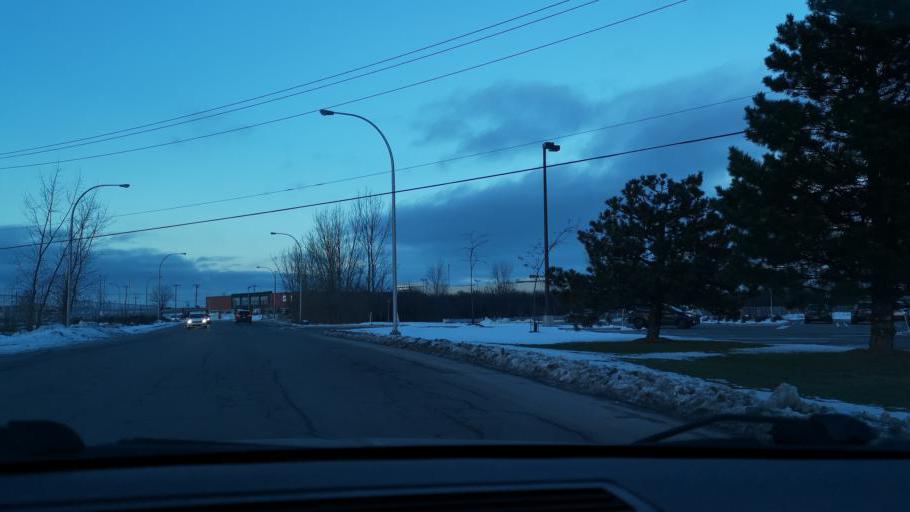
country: CA
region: Quebec
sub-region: Laval
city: Laval
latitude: 45.5756
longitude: -73.7569
